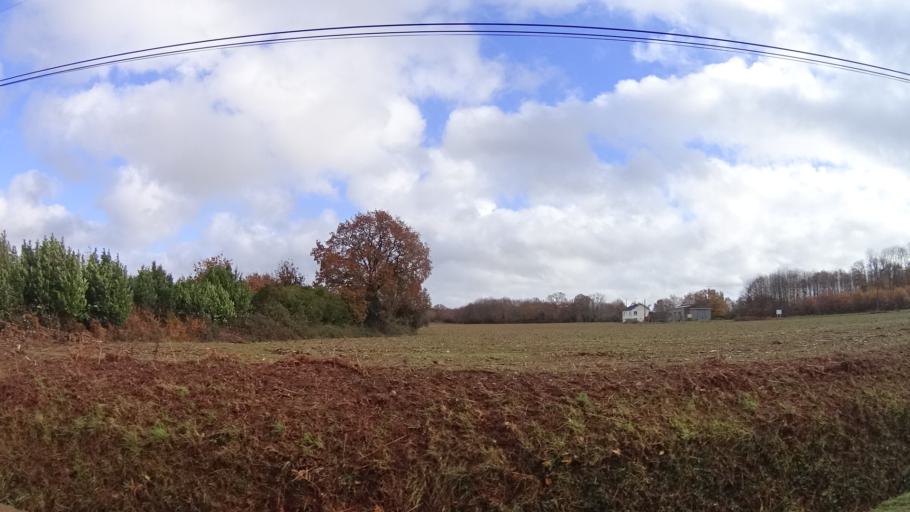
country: FR
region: Pays de la Loire
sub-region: Departement de la Loire-Atlantique
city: Fegreac
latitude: 47.5969
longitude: -2.0685
